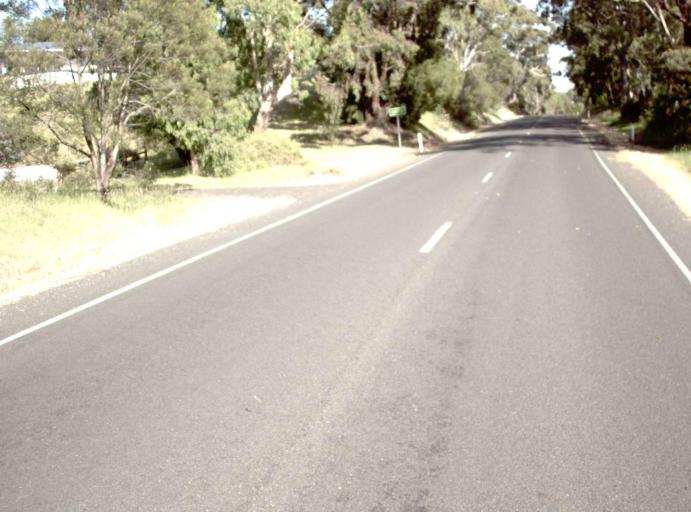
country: AU
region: Victoria
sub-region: East Gippsland
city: Lakes Entrance
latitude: -37.8773
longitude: 147.8516
